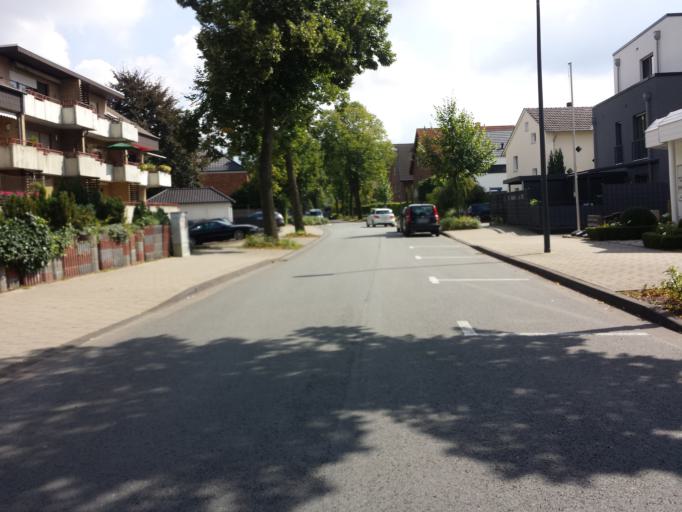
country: DE
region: North Rhine-Westphalia
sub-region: Regierungsbezirk Detmold
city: Guetersloh
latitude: 51.8931
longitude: 8.3677
